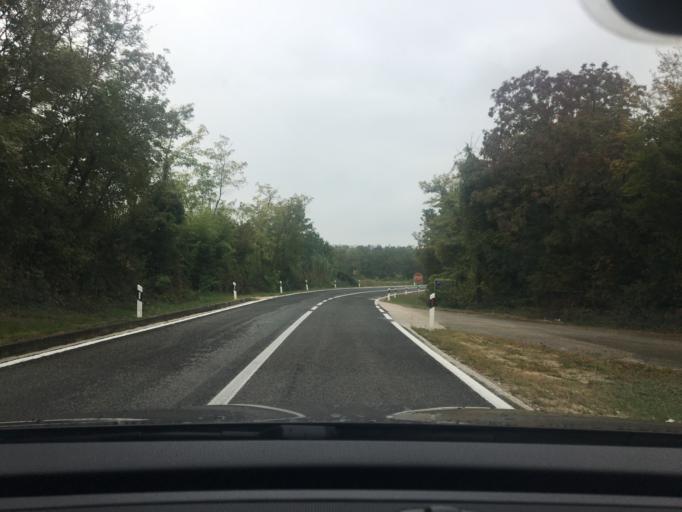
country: HR
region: Istarska
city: Buje
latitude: 45.4342
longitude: 13.6577
